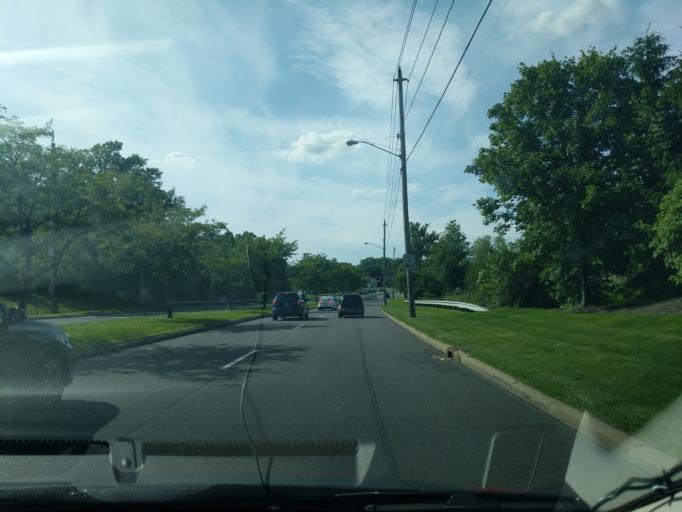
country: US
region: Ohio
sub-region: Cuyahoga County
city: Warrensville Heights
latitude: 41.4454
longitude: -81.5311
